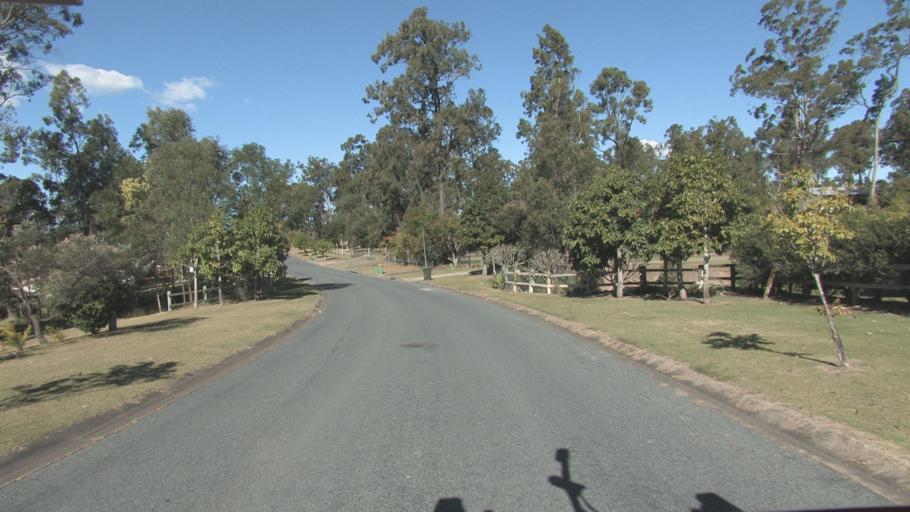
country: AU
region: Queensland
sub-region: Ipswich
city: Springfield Lakes
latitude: -27.7250
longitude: 152.9201
